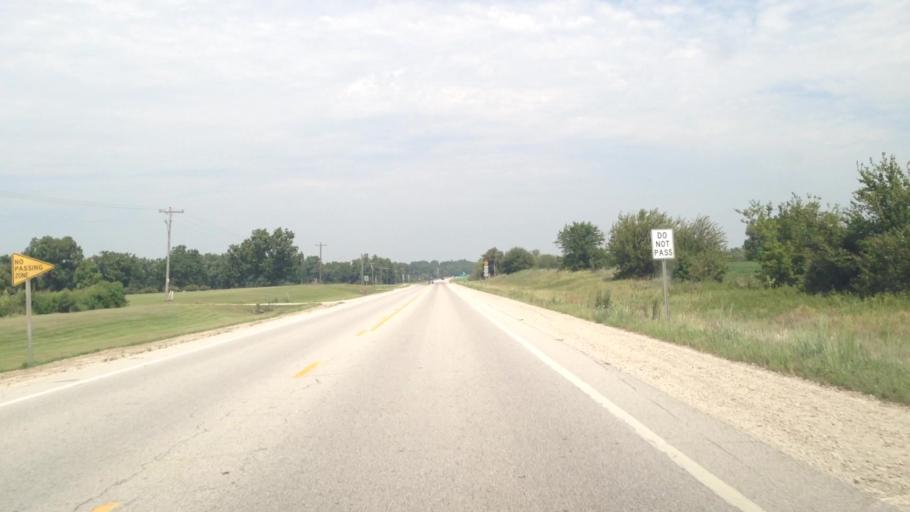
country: US
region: Kansas
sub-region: Neosho County
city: Erie
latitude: 37.5255
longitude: -95.2702
